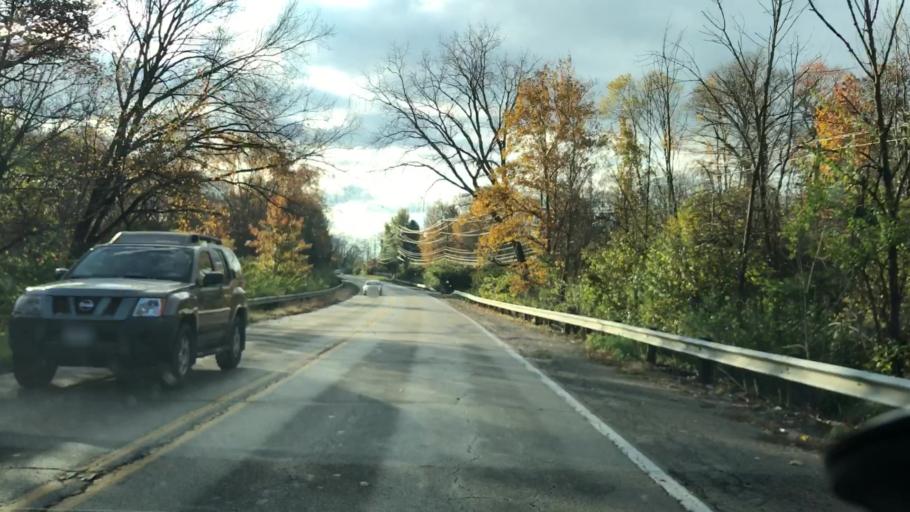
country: US
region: Ohio
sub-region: Franklin County
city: Upper Arlington
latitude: 40.0198
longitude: -83.1012
